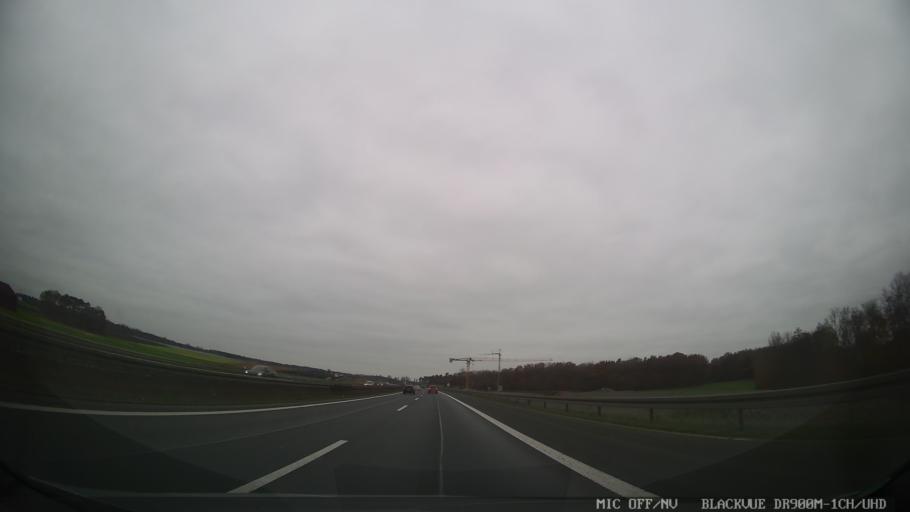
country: DE
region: Bavaria
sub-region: Regierungsbezirk Unterfranken
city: Kleinlangheim
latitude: 49.7844
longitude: 10.2858
